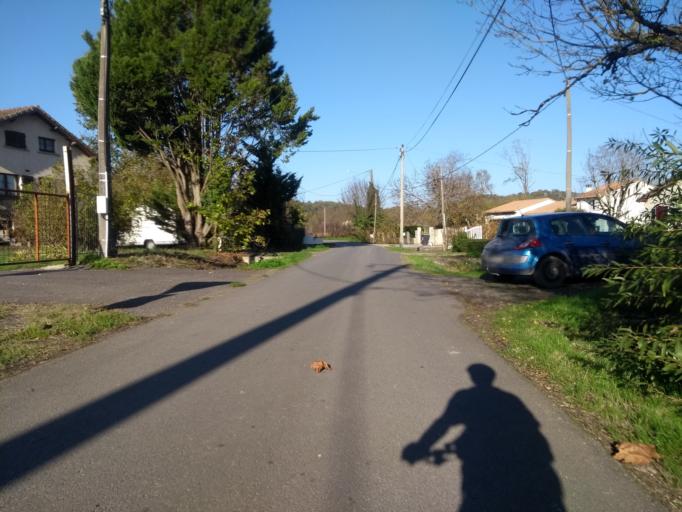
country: FR
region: Aquitaine
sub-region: Departement de la Gironde
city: Cambes
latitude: 44.7271
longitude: -0.4749
